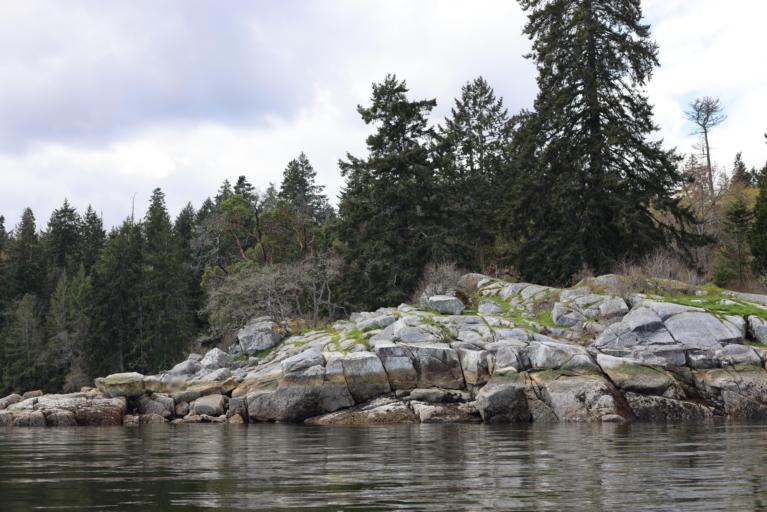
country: CA
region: British Columbia
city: North Saanich
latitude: 48.6322
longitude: -123.5286
